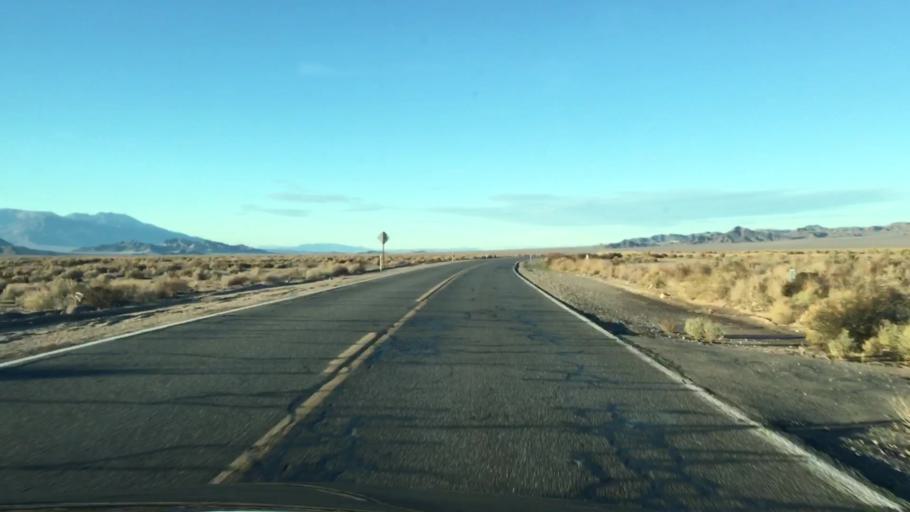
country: US
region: California
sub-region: San Bernardino County
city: Fort Irwin
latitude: 35.2929
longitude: -116.0822
